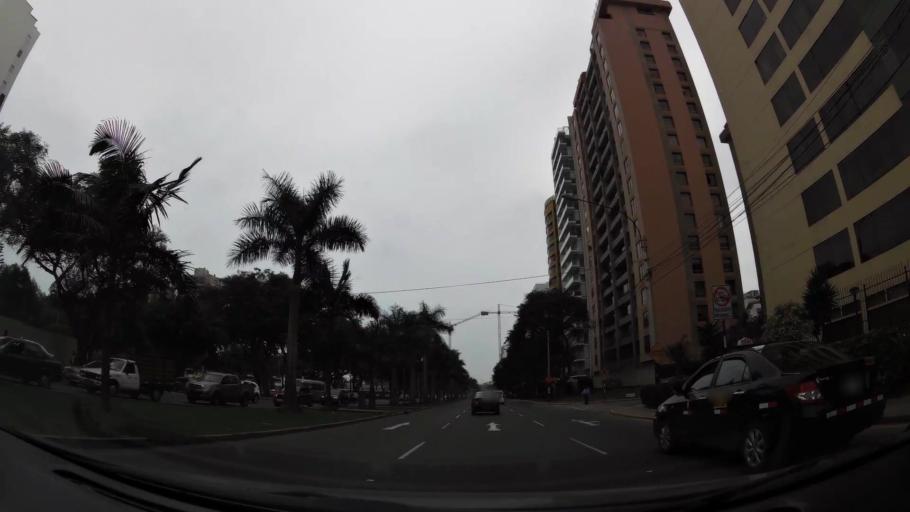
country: PE
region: Lima
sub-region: Lima
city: San Isidro
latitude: -12.0943
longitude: -77.0481
